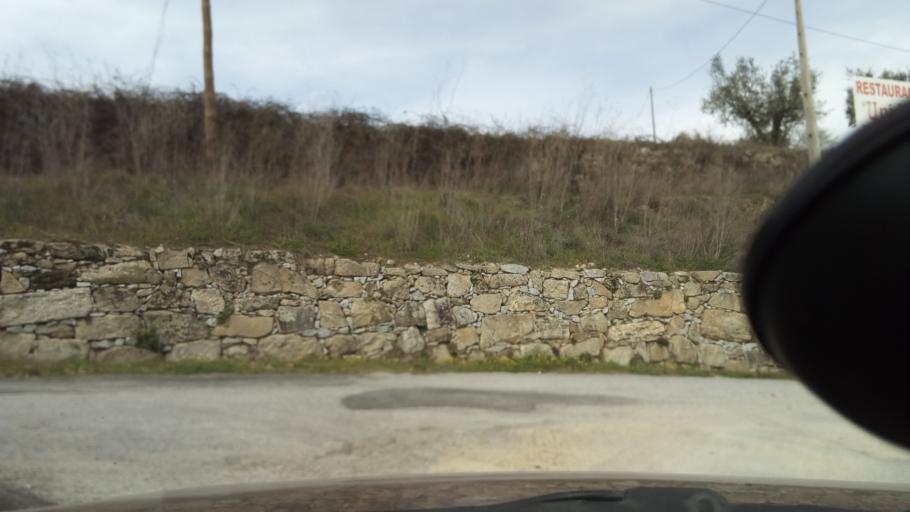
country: PT
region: Guarda
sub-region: Fornos de Algodres
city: Fornos de Algodres
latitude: 40.6132
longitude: -7.5381
